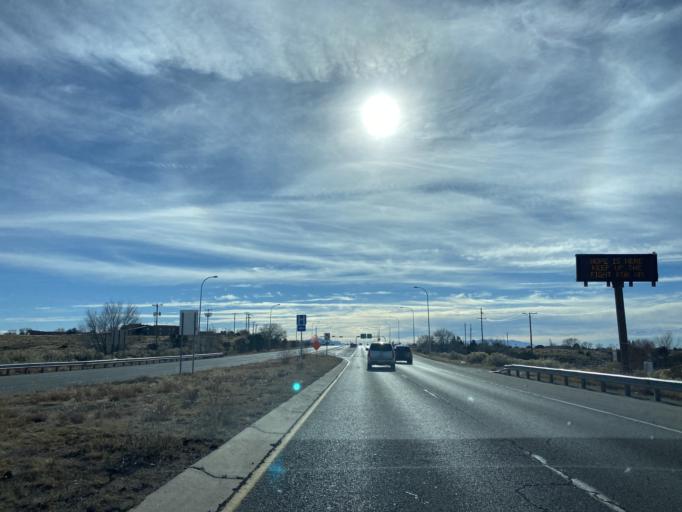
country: US
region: New Mexico
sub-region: Santa Fe County
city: Agua Fria
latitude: 35.6158
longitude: -106.0317
